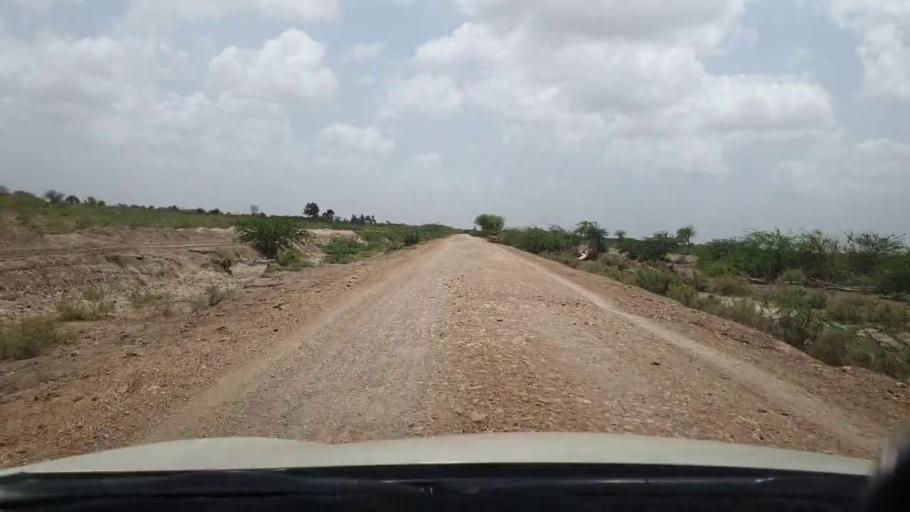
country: PK
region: Sindh
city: Kadhan
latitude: 24.3896
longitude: 68.9342
